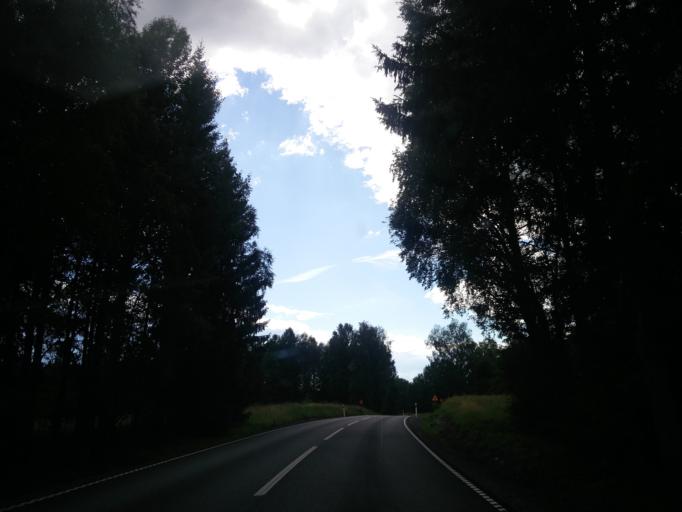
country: SE
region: OErebro
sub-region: Hallefors Kommun
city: Haellefors
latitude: 59.8058
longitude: 14.6027
